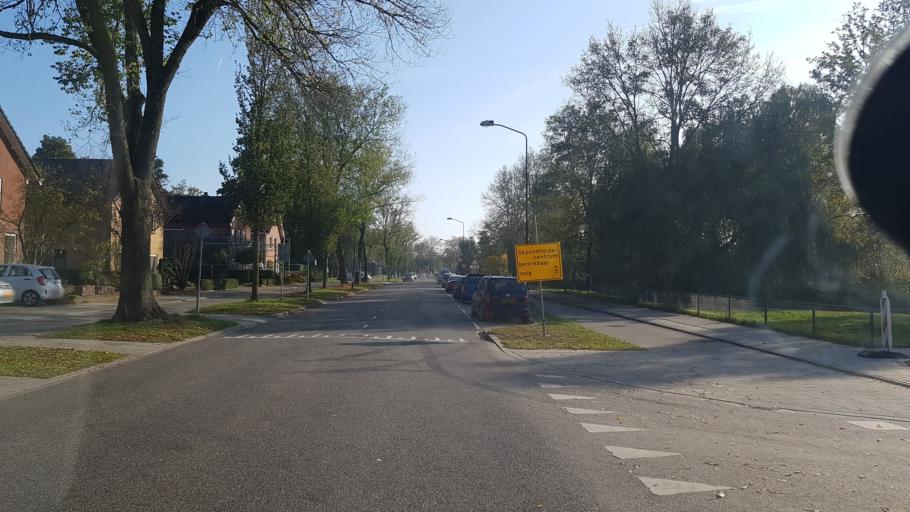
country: NL
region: Gelderland
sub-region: Gemeente Apeldoorn
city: Apeldoorn
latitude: 52.2314
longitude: 5.9911
